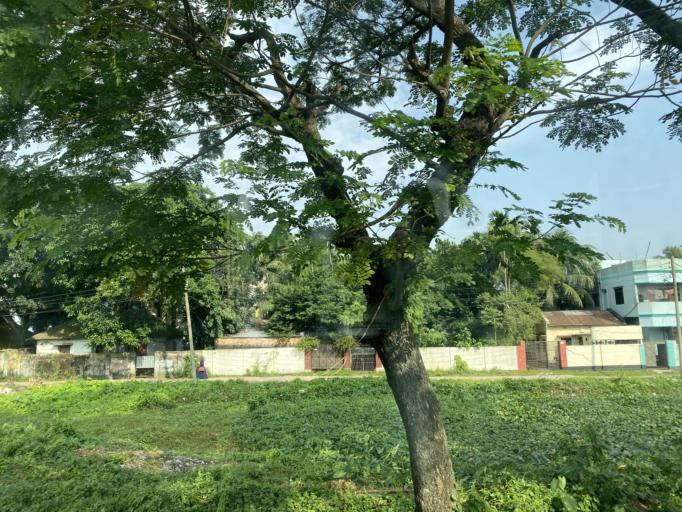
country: BD
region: Dhaka
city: Bhairab Bazar
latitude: 23.9679
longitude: 91.1127
